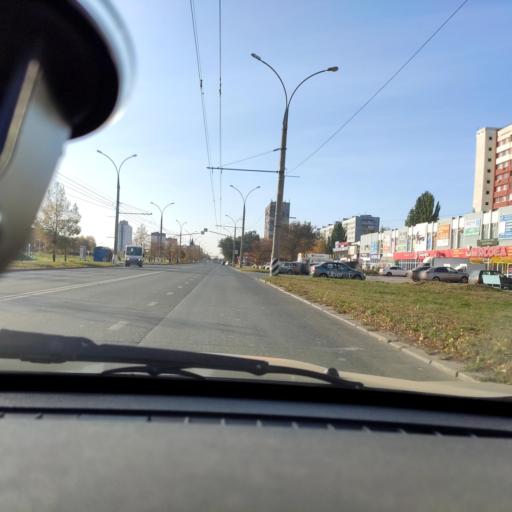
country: RU
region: Samara
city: Tol'yatti
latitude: 53.5125
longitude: 49.2719
